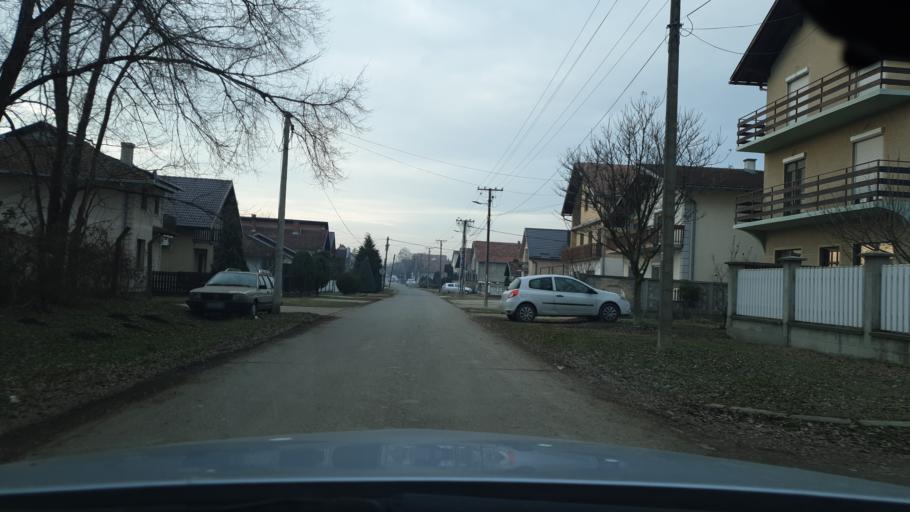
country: RS
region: Autonomna Pokrajina Vojvodina
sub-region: Sremski Okrug
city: Stara Pazova
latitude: 44.9890
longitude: 20.1853
